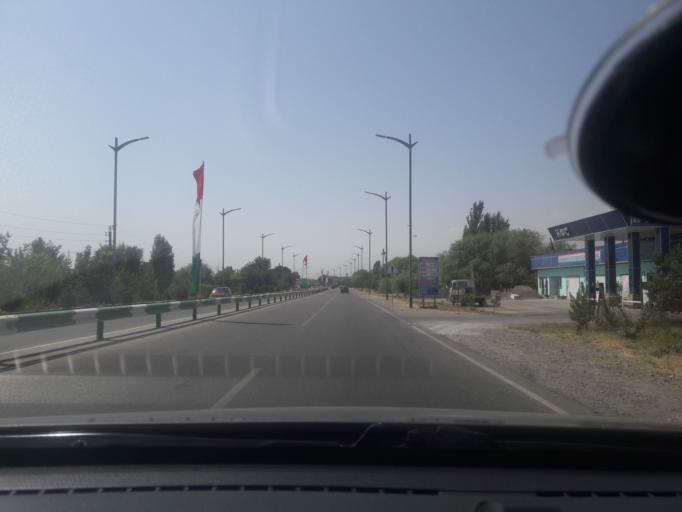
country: TJ
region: Republican Subordination
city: Hisor
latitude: 38.5608
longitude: 68.4483
